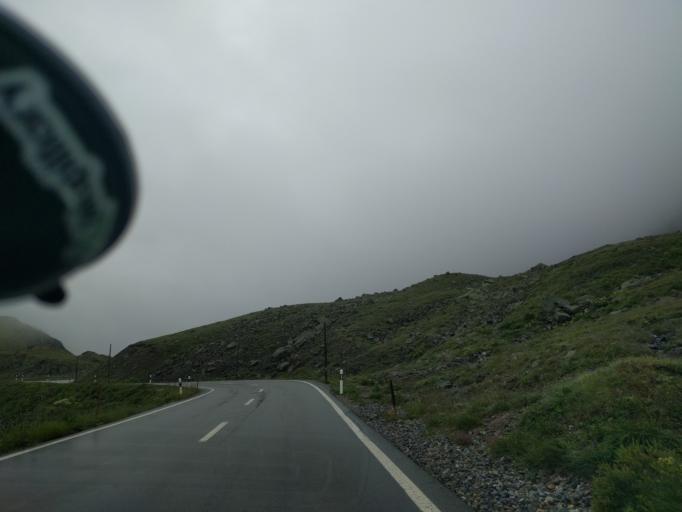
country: CH
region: Grisons
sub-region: Praettigau/Davos District
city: Davos
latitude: 46.7562
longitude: 9.9396
